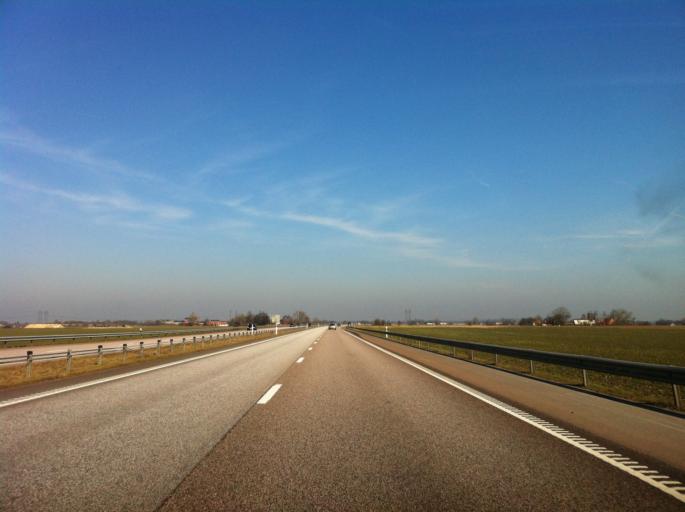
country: SE
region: Skane
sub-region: Angelholms Kommun
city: Strovelstorp
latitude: 56.1130
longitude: 12.8121
